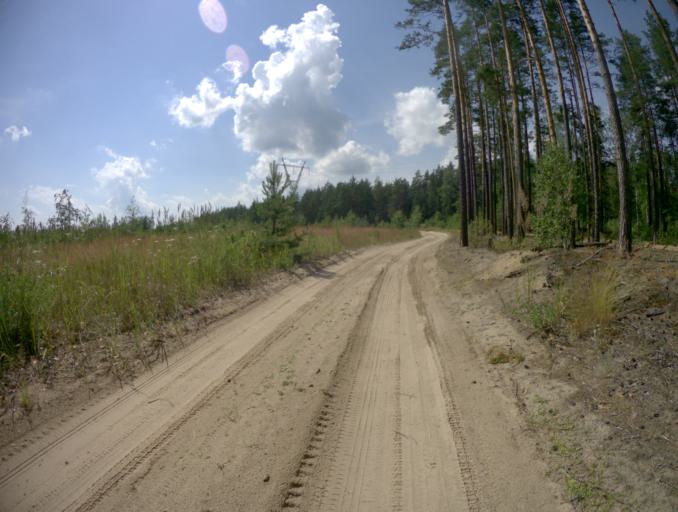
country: RU
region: Ivanovo
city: Yuzha
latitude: 56.5155
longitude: 42.1561
